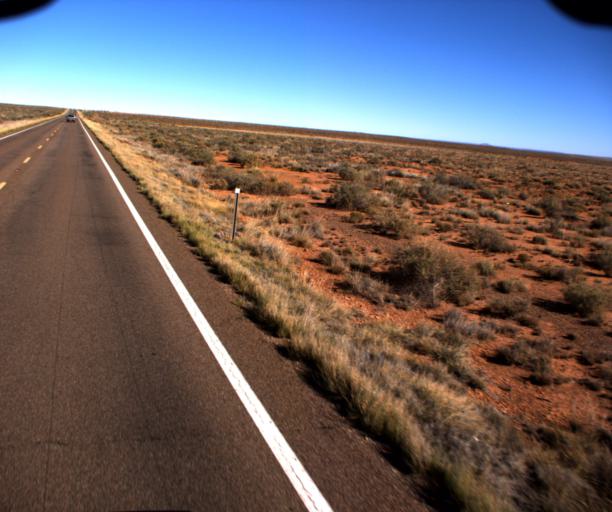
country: US
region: Arizona
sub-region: Navajo County
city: Holbrook
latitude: 34.7280
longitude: -110.1160
